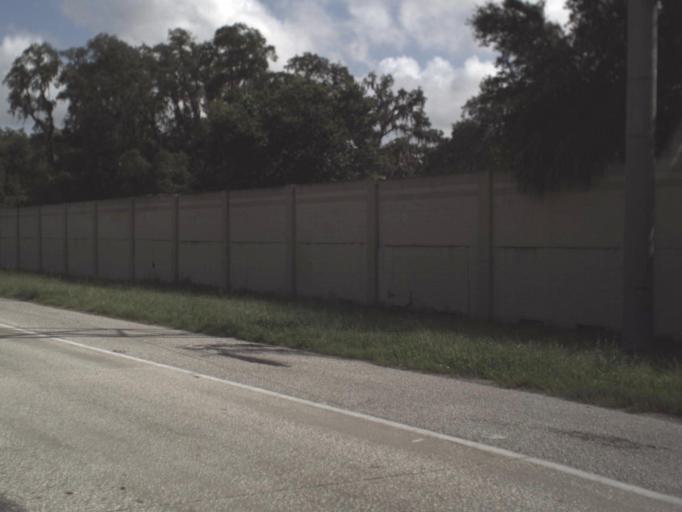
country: US
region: Florida
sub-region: Hillsborough County
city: University
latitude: 28.0654
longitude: -82.4546
